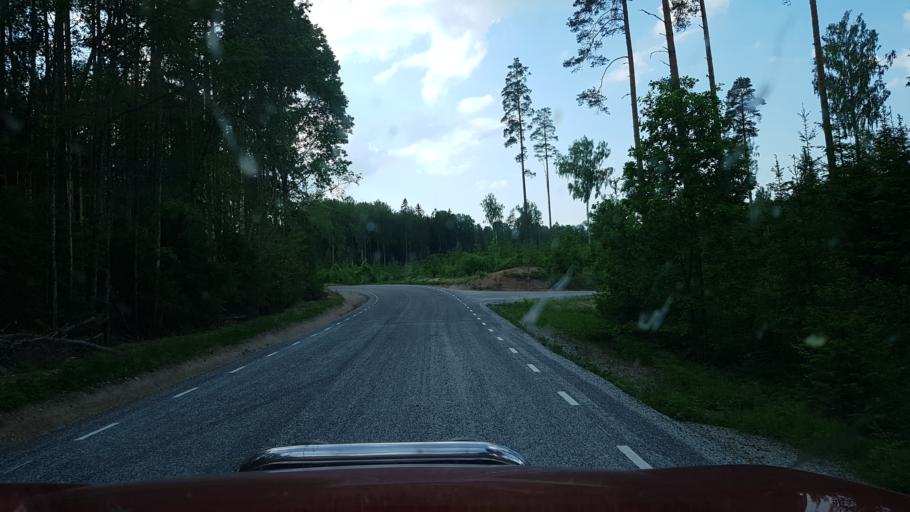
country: EE
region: Tartu
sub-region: UElenurme vald
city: Ulenurme
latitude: 58.0953
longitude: 26.8047
